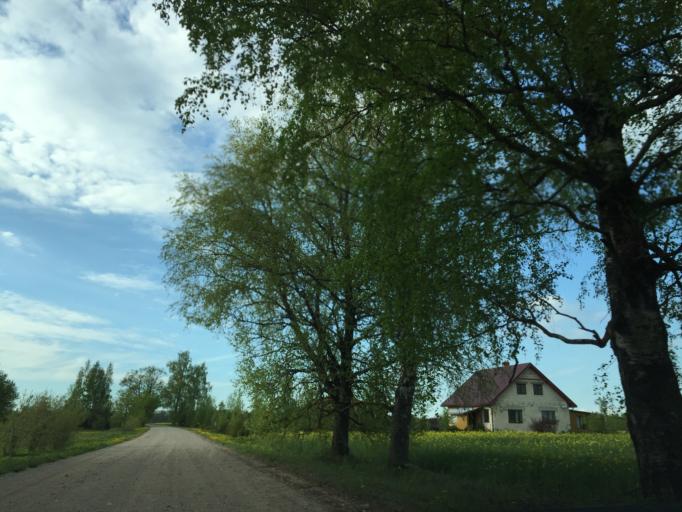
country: LV
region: Limbazu Rajons
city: Limbazi
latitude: 57.3690
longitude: 24.6914
